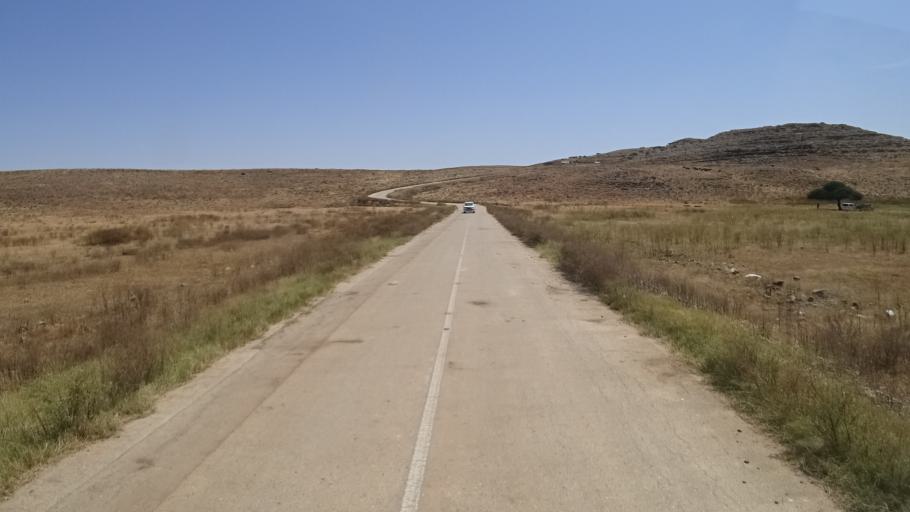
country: OM
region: Zufar
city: Salalah
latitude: 17.1549
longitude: 54.6195
